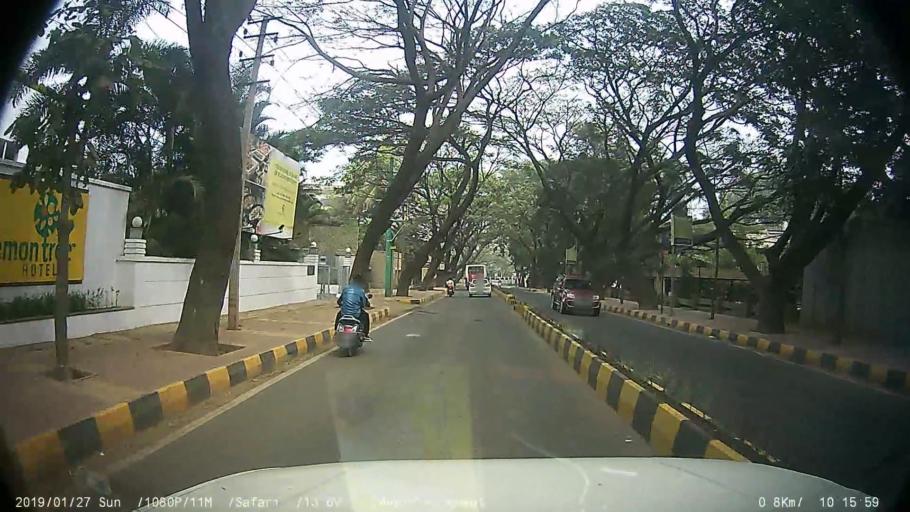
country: IN
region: Karnataka
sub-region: Bangalore Urban
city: Anekal
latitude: 12.8406
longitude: 77.6600
